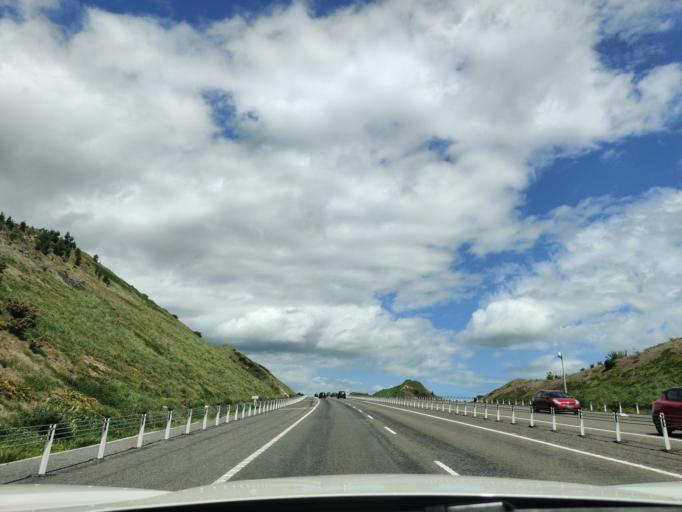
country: NZ
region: Wellington
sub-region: Porirua City
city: Porirua
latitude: -41.0708
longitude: 174.9420
